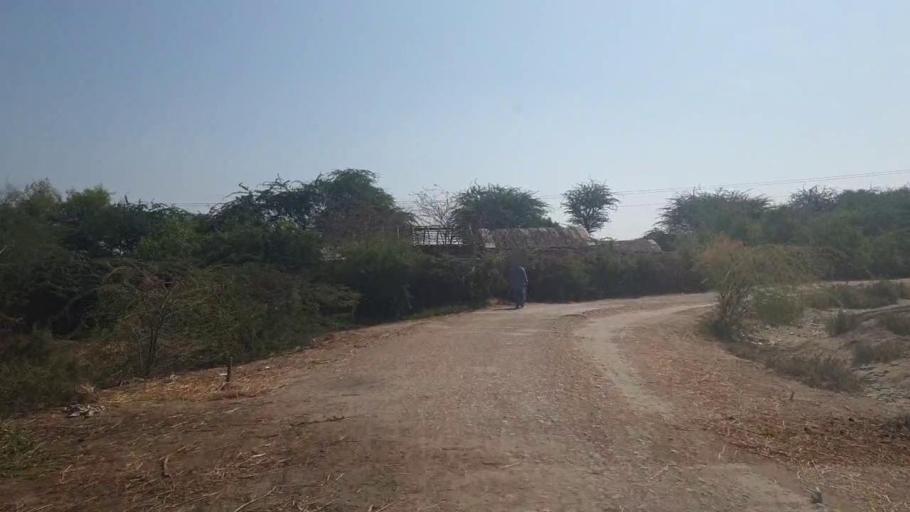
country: PK
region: Sindh
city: Badin
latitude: 24.6386
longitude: 68.9140
